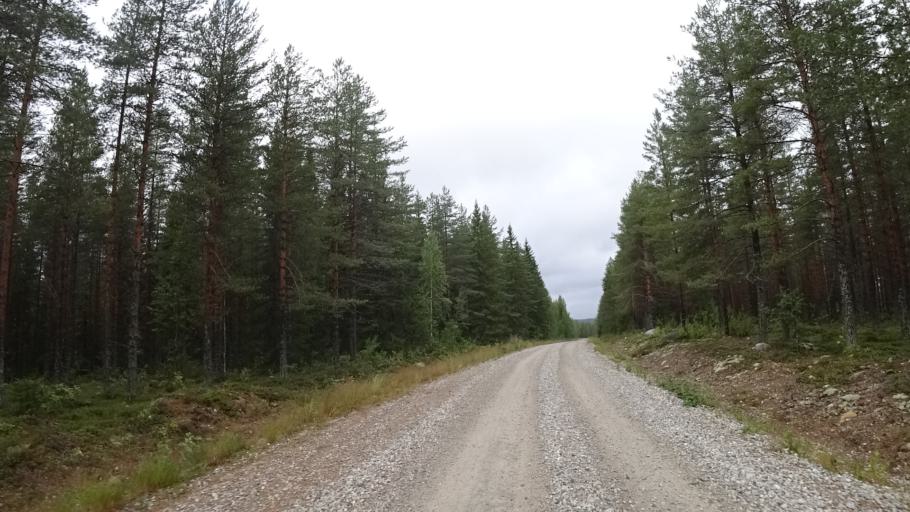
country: FI
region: North Karelia
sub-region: Pielisen Karjala
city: Lieksa
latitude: 63.4746
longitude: 30.2650
